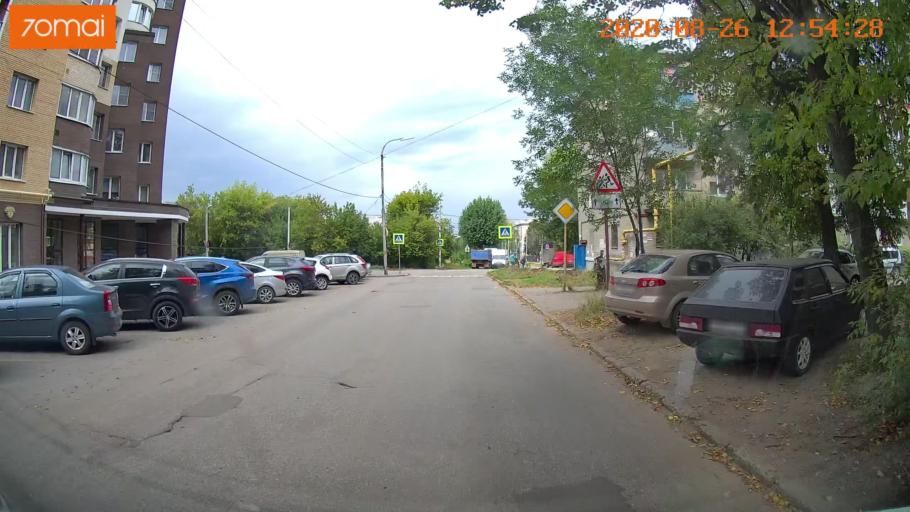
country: RU
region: Rjazan
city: Ryazan'
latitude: 54.6061
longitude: 39.7587
